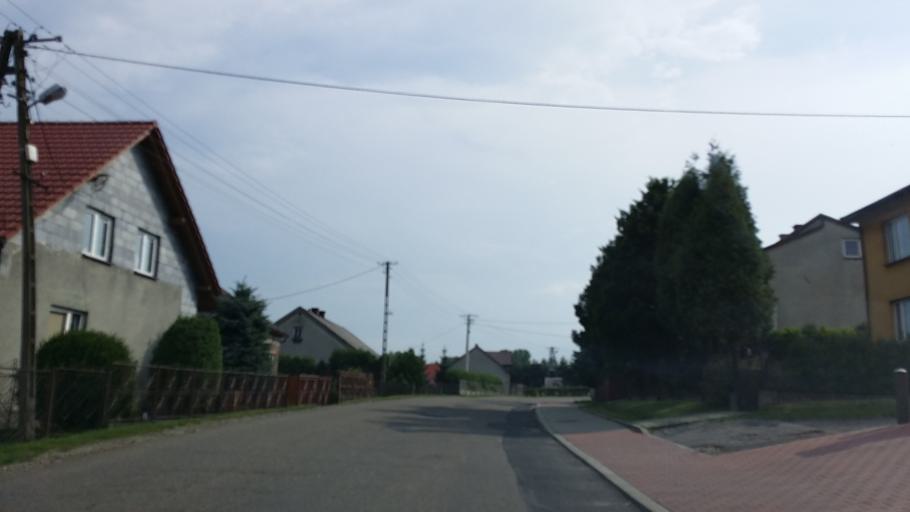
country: PL
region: Lesser Poland Voivodeship
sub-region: Powiat wadowicki
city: Bachowice
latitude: 49.9759
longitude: 19.5020
